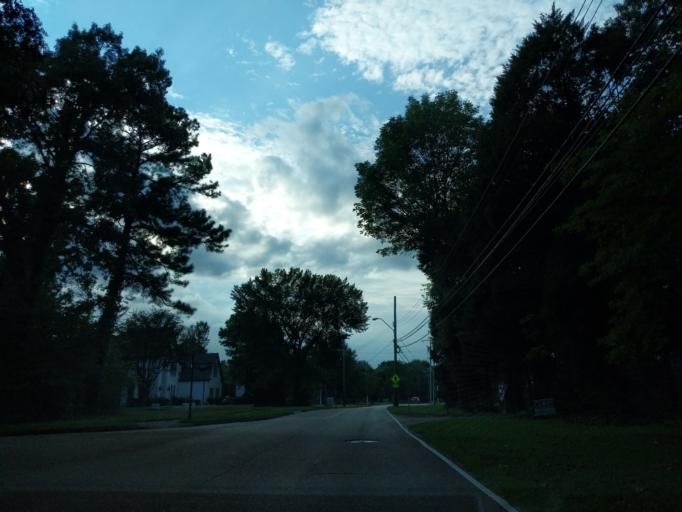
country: US
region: Tennessee
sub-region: Shelby County
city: Germantown
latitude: 35.0638
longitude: -89.7659
